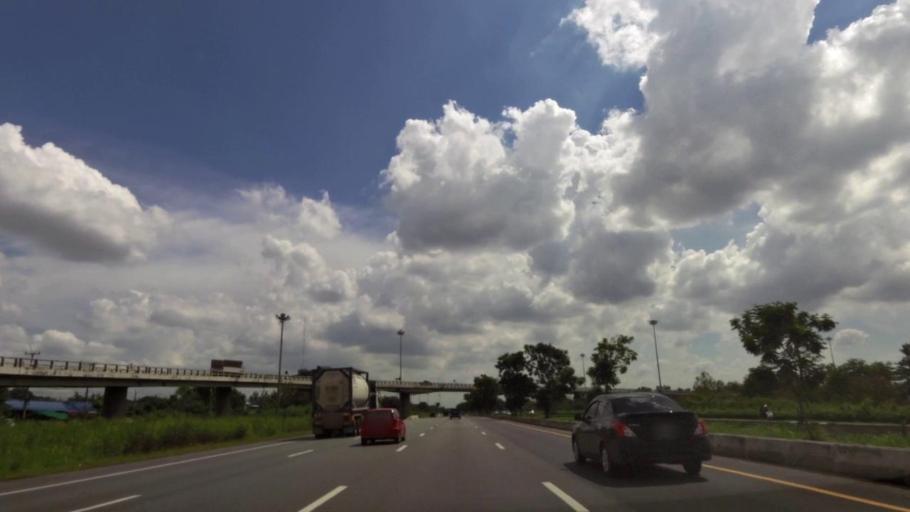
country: TH
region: Phra Nakhon Si Ayutthaya
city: Bang Pahan
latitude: 14.4514
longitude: 100.5406
